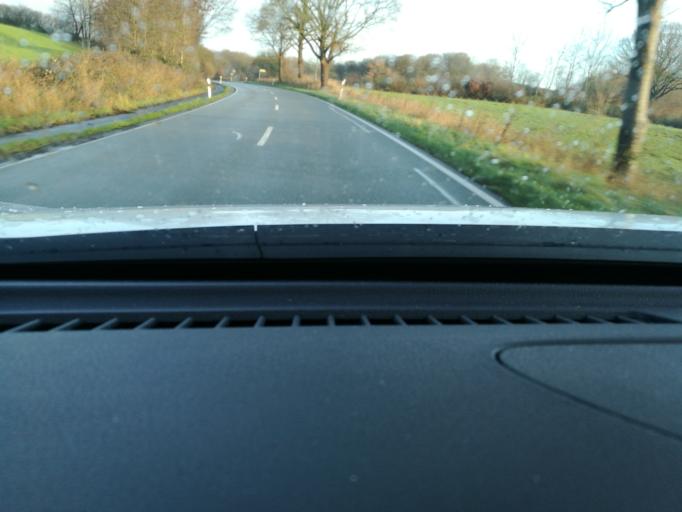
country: DE
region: Schleswig-Holstein
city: Ascheffel
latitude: 54.4154
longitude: 9.7030
